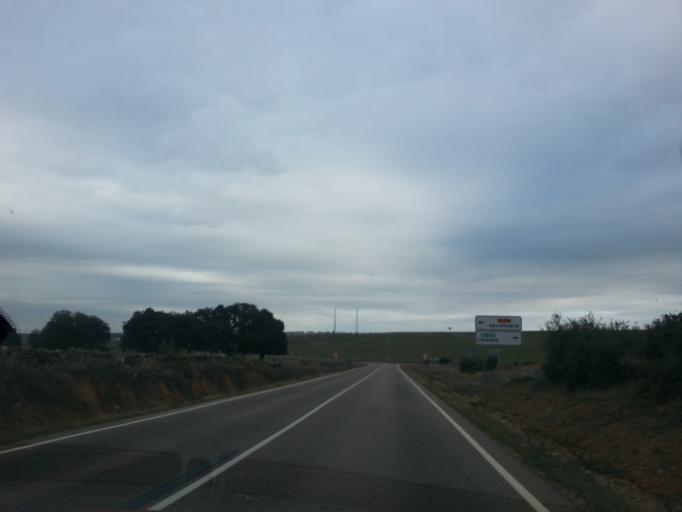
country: ES
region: Castille and Leon
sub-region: Provincia de Salamanca
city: Vecinos
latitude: 40.7685
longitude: -5.8857
